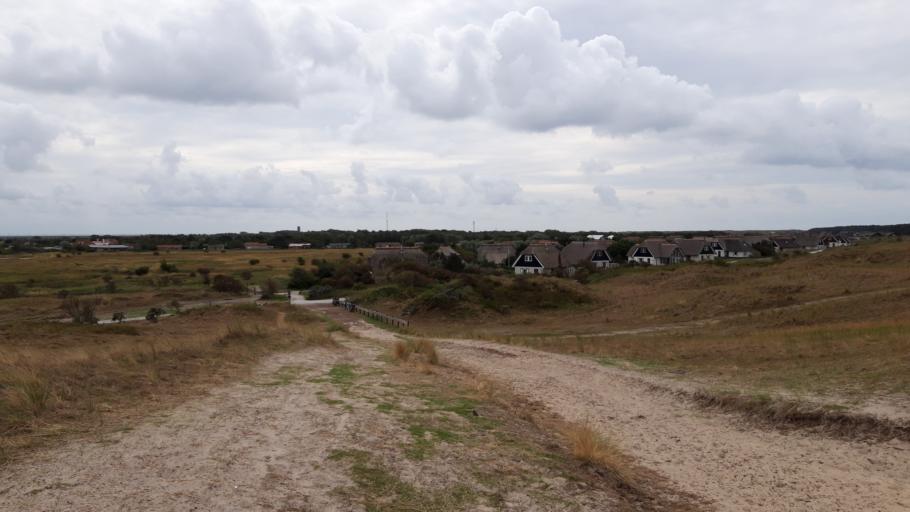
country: NL
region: Friesland
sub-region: Gemeente Ameland
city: Hollum
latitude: 53.4556
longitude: 5.6411
